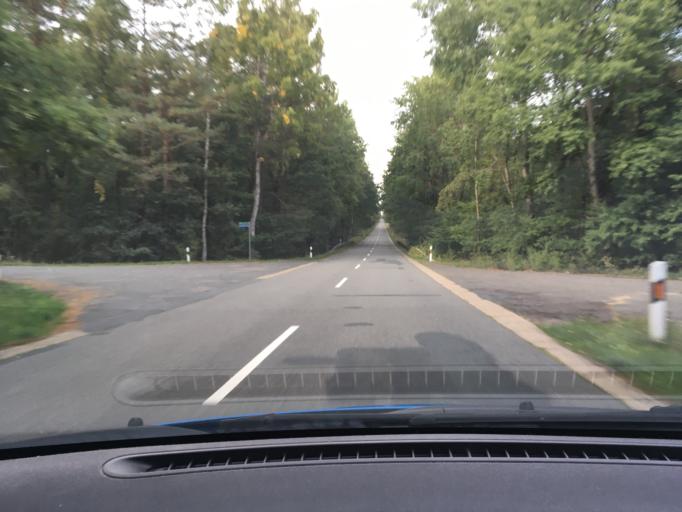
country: DE
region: Lower Saxony
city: Bispingen
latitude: 53.0784
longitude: 10.0346
